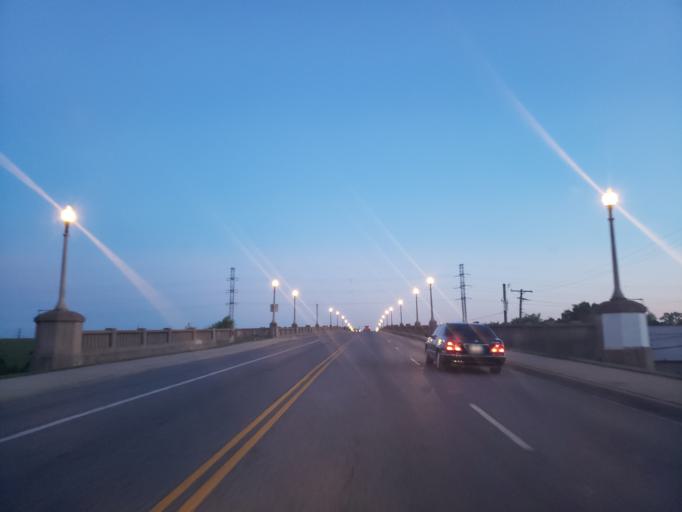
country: US
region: Texas
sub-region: Dallas County
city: Dallas
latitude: 32.7592
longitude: -96.7943
